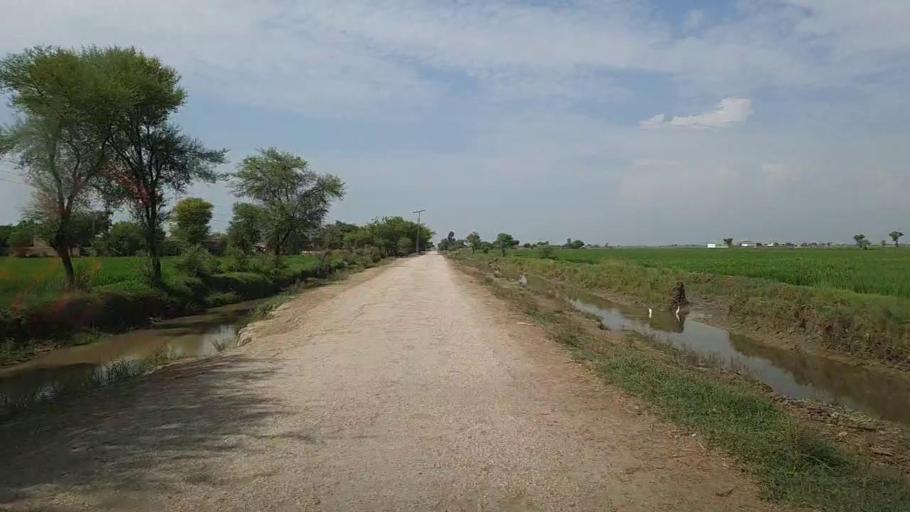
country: PK
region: Sindh
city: Thul
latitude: 28.2493
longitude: 68.8085
